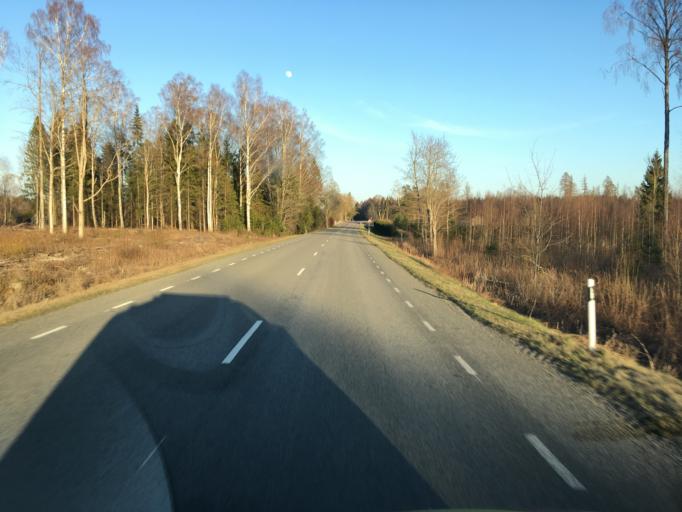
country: EE
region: Raplamaa
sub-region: Rapla vald
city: Rapla
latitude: 59.0696
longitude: 24.9097
